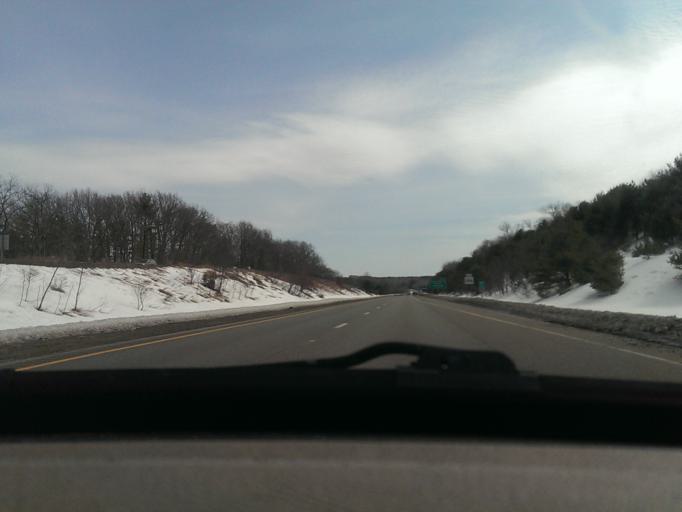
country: US
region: Massachusetts
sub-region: Worcester County
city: East Douglas
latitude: 42.0968
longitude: -71.7016
